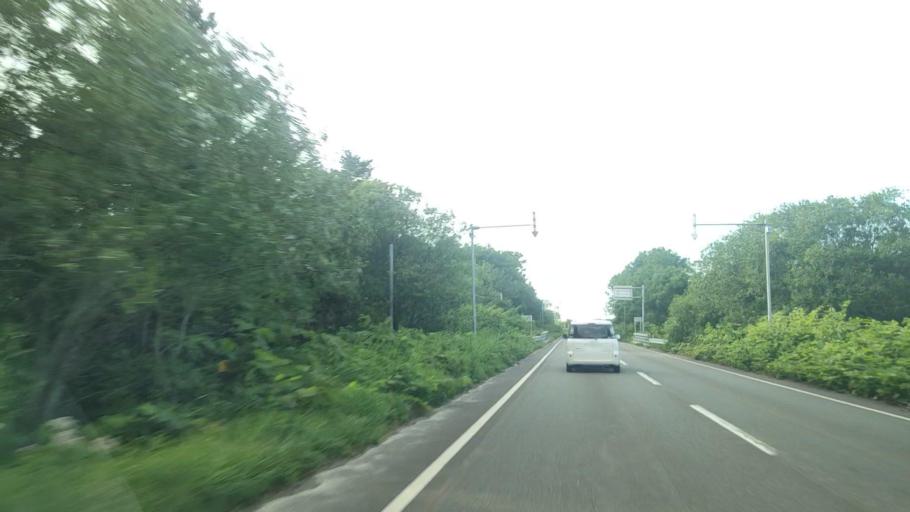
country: JP
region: Hokkaido
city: Makubetsu
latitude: 45.0520
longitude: 141.7504
